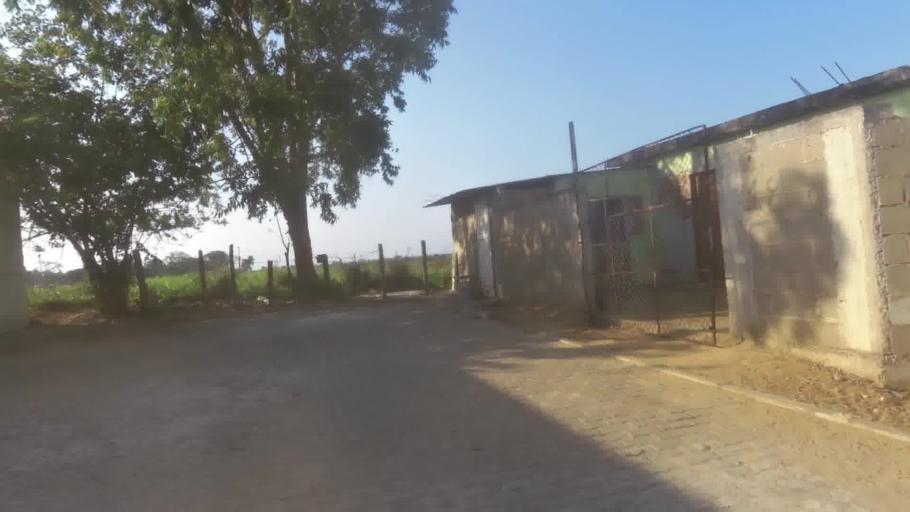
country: BR
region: Espirito Santo
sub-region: Itapemirim
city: Itapemirim
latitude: -21.0167
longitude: -40.8183
